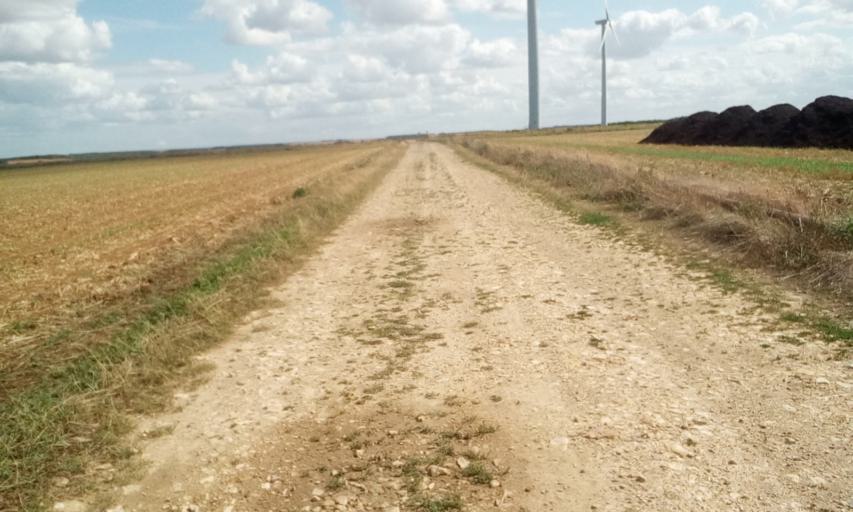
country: FR
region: Lower Normandy
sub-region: Departement du Calvados
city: Bellengreville
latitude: 49.0974
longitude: -0.2272
